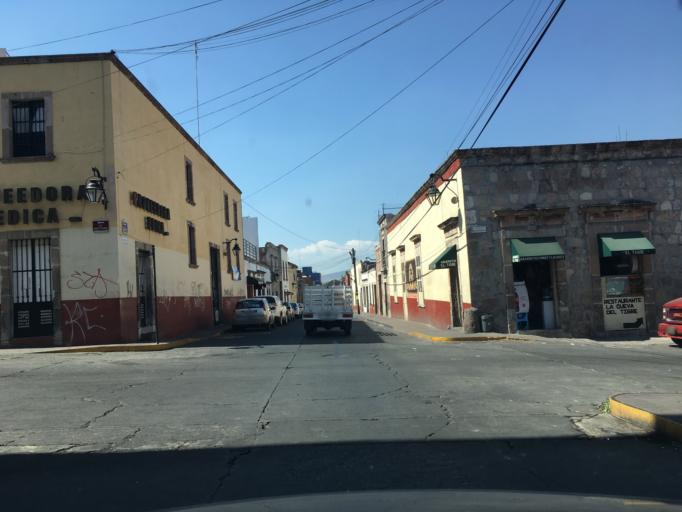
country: MX
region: Michoacan
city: Morelia
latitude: 19.7056
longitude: -101.1930
